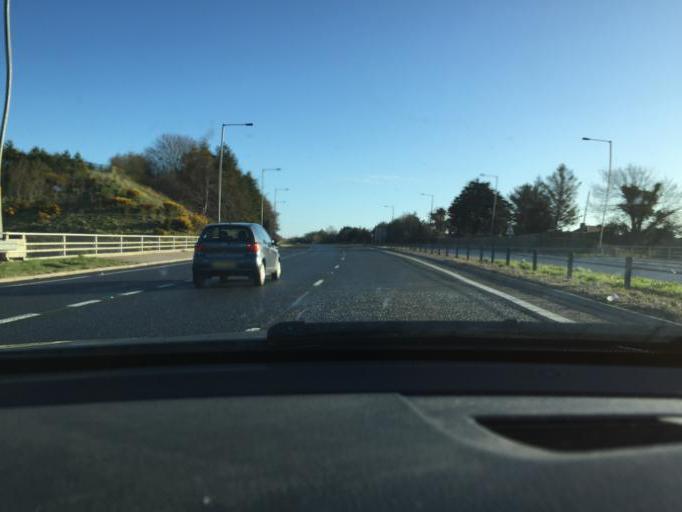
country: GB
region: Northern Ireland
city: Moira
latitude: 54.4059
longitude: -6.1667
